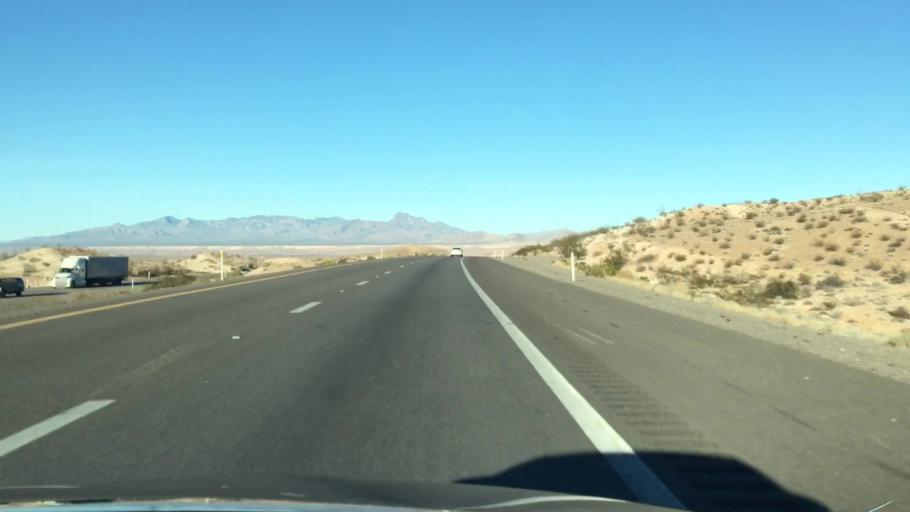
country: US
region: Nevada
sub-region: Clark County
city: Moapa Town
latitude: 36.5987
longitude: -114.6408
